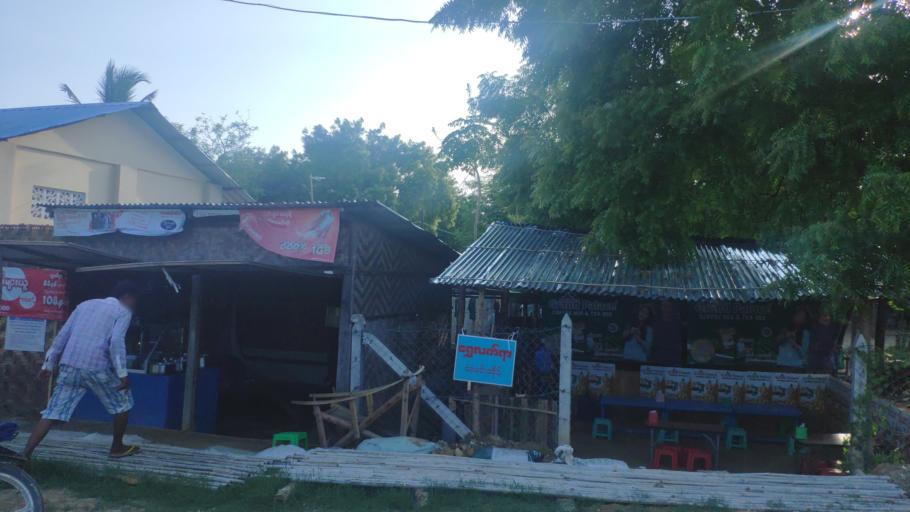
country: MM
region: Mandalay
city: Meiktila
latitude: 20.9040
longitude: 95.8632
